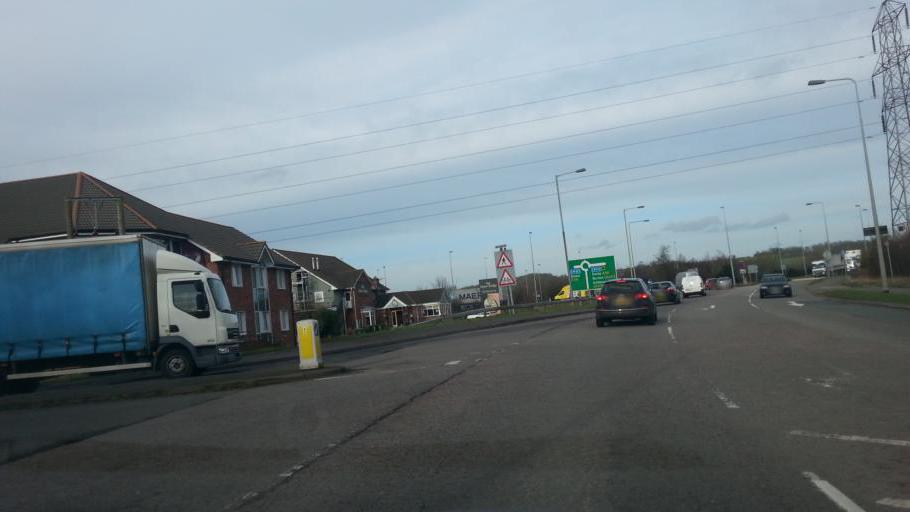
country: GB
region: England
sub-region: Staffordshire
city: Uttoxeter
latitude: 52.9063
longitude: -1.8545
